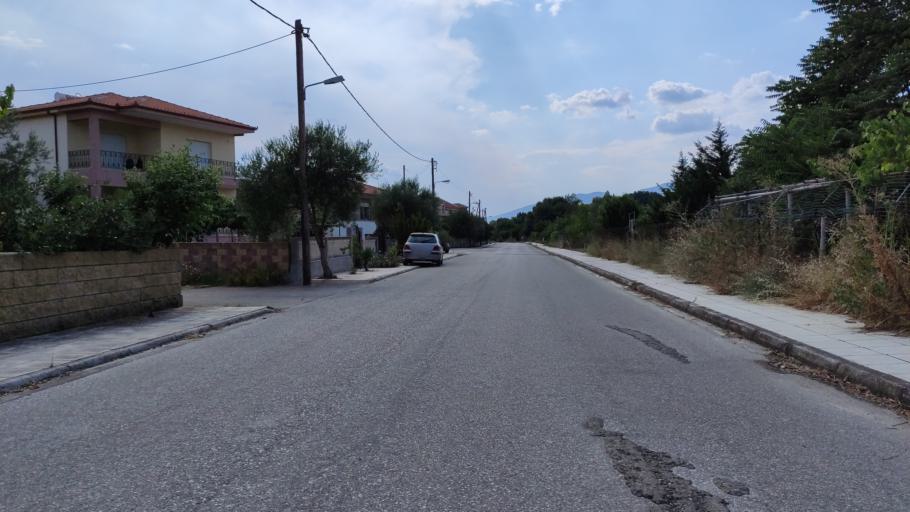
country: GR
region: East Macedonia and Thrace
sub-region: Nomos Rodopis
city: Komotini
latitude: 41.1329
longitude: 25.3961
